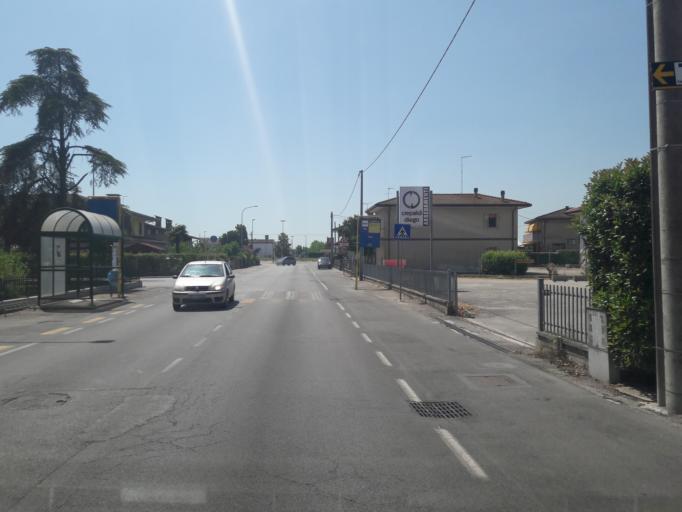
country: IT
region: Veneto
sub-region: Provincia di Rovigo
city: Taglio di Po
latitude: 44.9993
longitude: 12.2106
